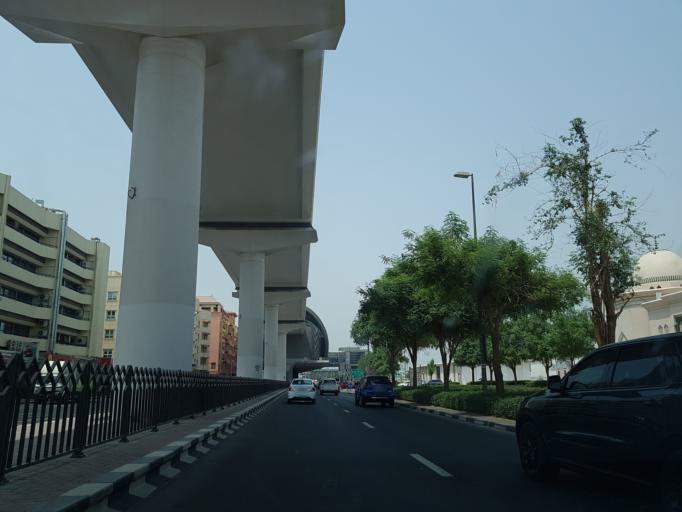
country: AE
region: Ash Shariqah
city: Sharjah
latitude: 25.2417
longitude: 55.3164
